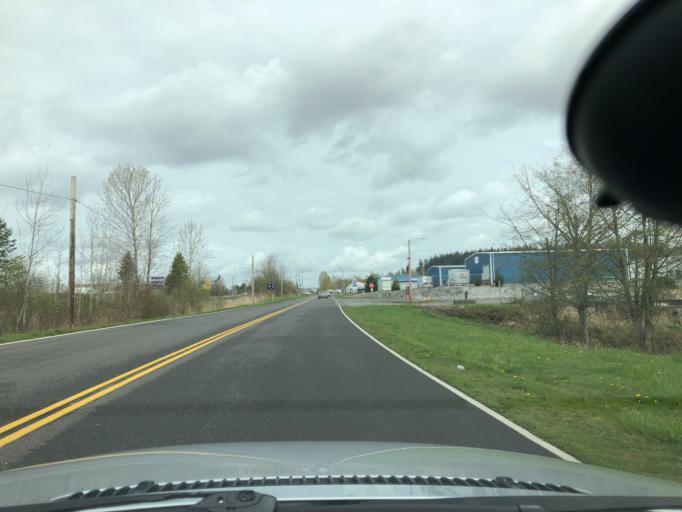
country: US
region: Washington
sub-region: Whatcom County
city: Blaine
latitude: 48.9872
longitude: -122.7344
